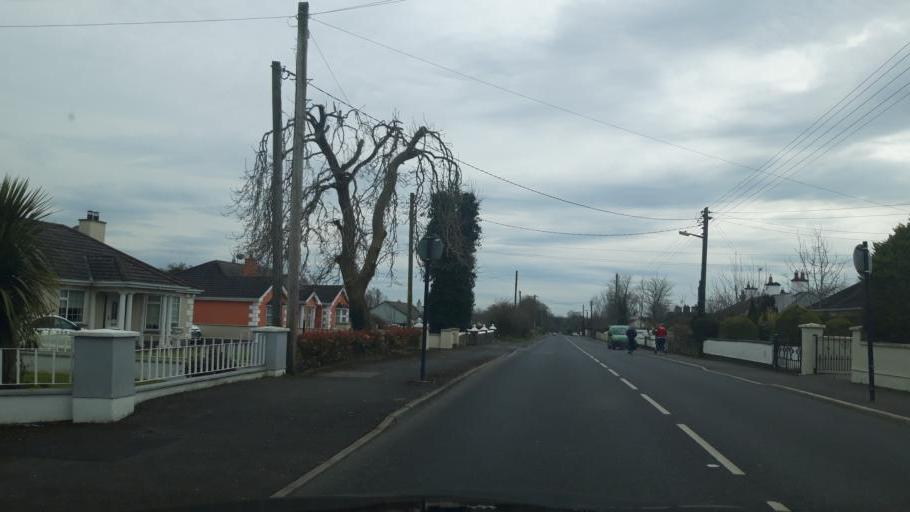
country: IE
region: Leinster
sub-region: Uibh Fhaili
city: Edenderry
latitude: 53.3387
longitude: -7.0439
